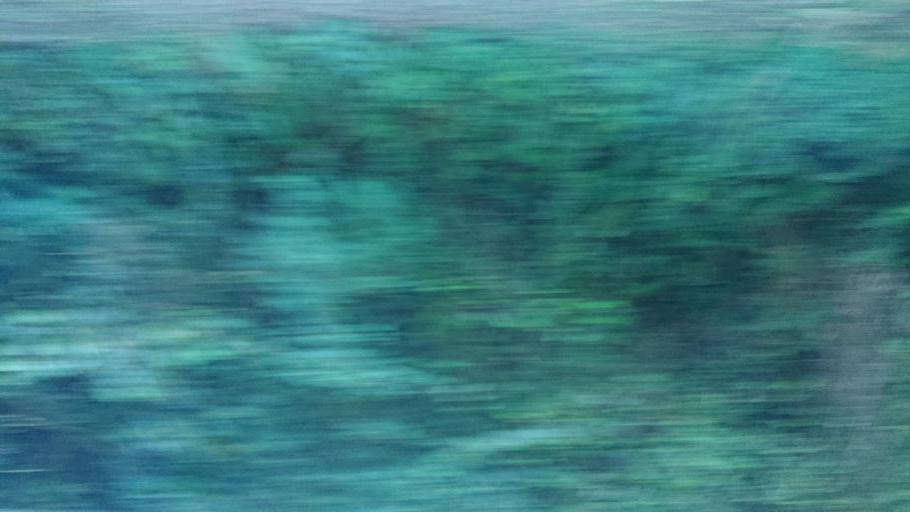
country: TW
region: Taiwan
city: Lugu
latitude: 23.4985
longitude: 120.7807
